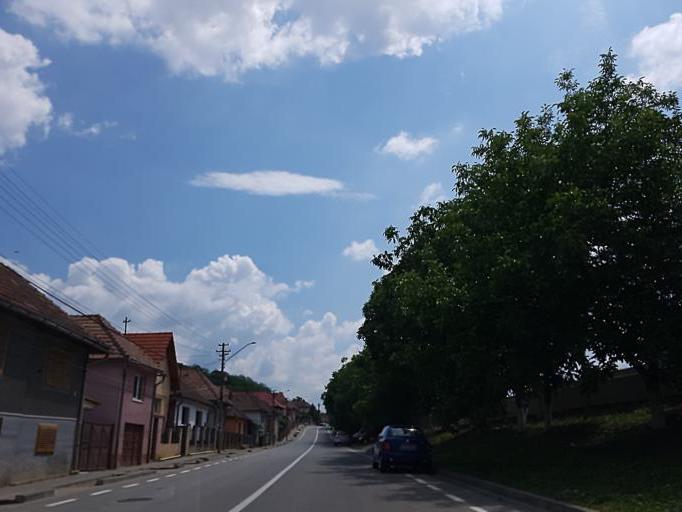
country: RO
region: Alba
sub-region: Municipiul Blaj
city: Veza
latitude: 46.1764
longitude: 23.9321
